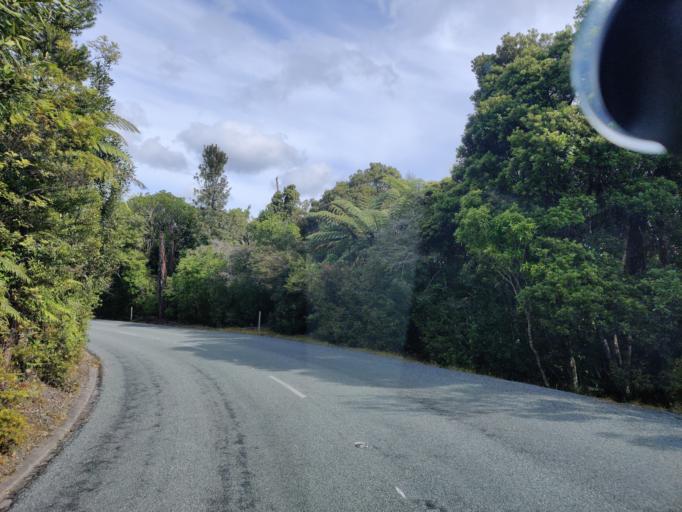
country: NZ
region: Northland
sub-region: Kaipara District
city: Dargaville
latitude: -35.6385
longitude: 173.5589
